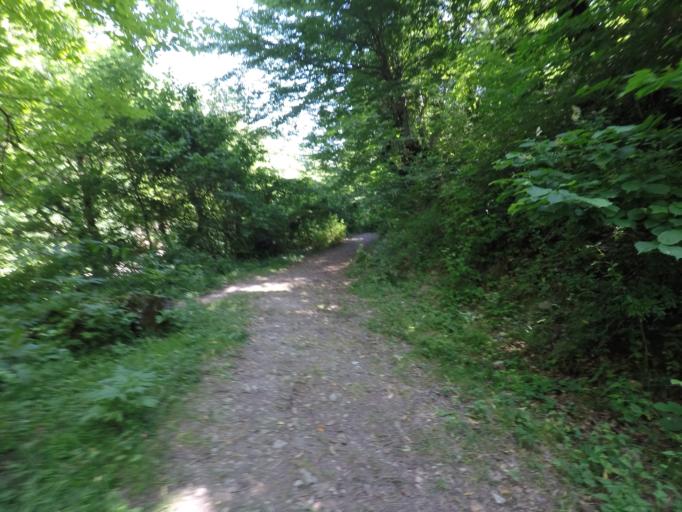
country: AZ
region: Qakh Rayon
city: Cinarli
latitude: 41.4912
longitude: 46.8582
